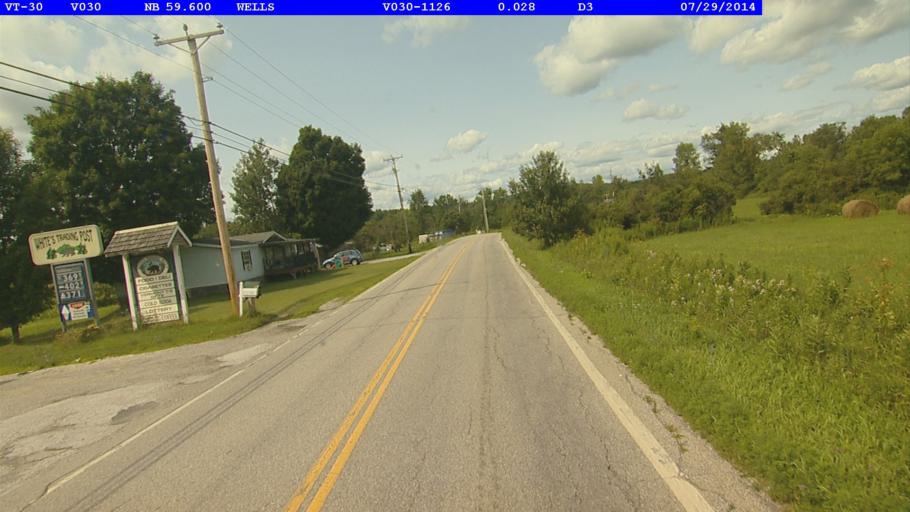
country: US
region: New York
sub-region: Washington County
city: Granville
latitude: 43.4083
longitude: -73.2263
